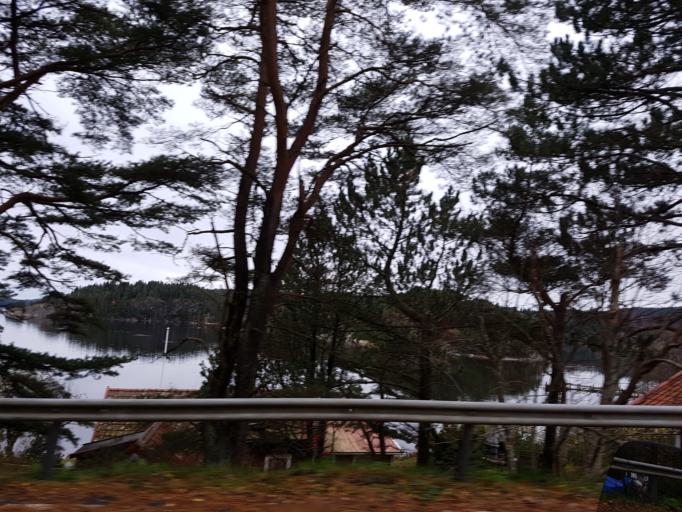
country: SE
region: Vaestra Goetaland
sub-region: Orust
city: Henan
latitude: 58.2993
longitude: 11.6890
